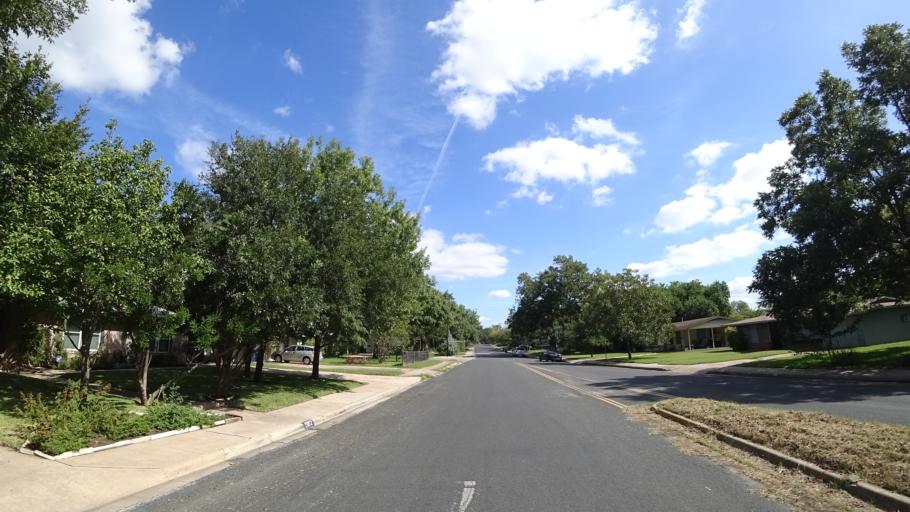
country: US
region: Texas
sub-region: Travis County
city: Austin
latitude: 30.3502
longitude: -97.7290
